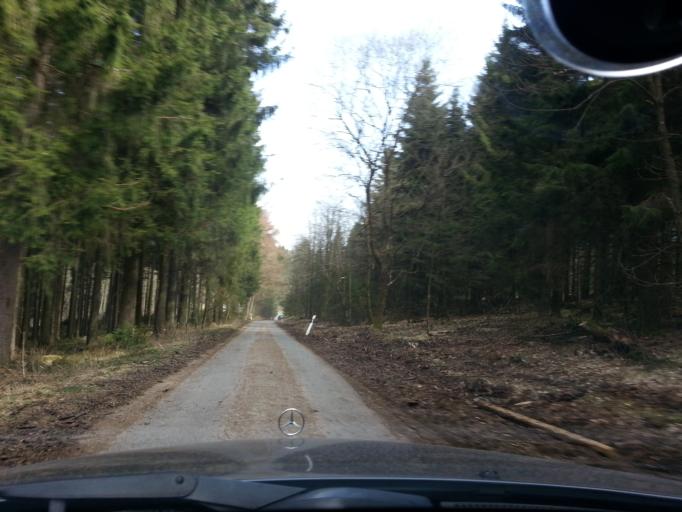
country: DE
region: North Rhine-Westphalia
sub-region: Regierungsbezirk Arnsberg
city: Bad Fredeburg
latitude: 51.2140
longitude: 8.3449
